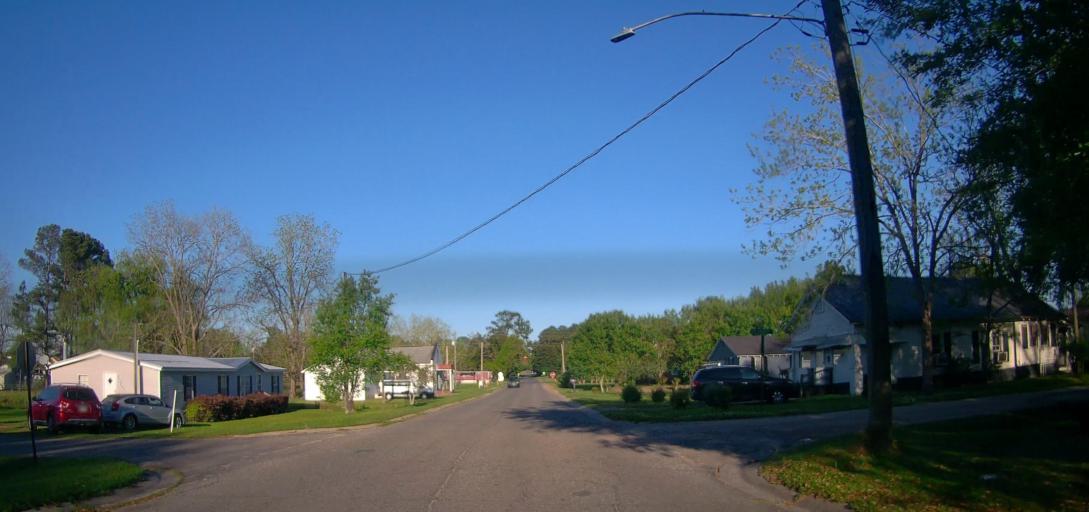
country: US
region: Georgia
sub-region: Ben Hill County
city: Fitzgerald
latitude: 31.7070
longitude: -83.2451
